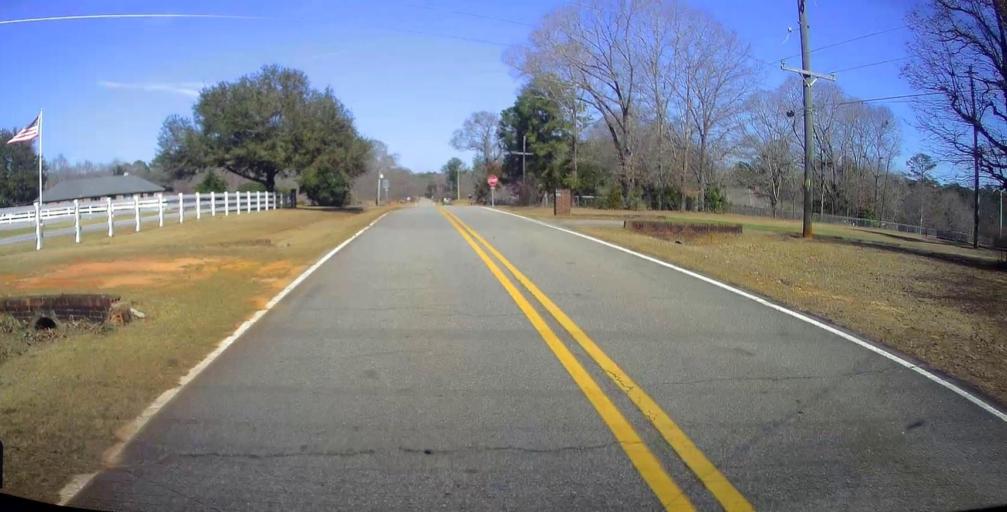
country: US
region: Georgia
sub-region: Houston County
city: Warner Robins
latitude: 32.5623
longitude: -83.6338
